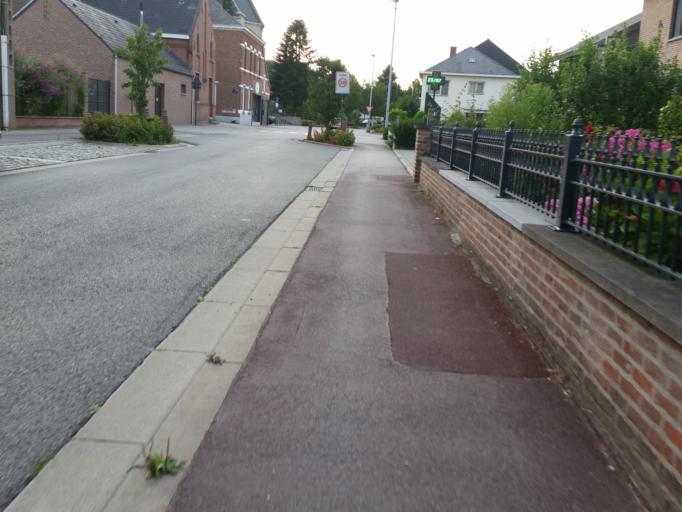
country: BE
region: Flanders
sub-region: Provincie Vlaams-Brabant
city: Zemst
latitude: 50.9834
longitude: 4.4667
